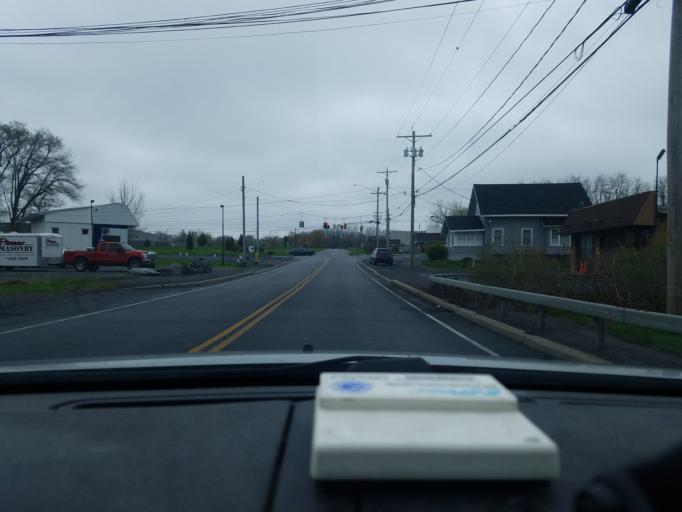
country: US
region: New York
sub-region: Onondaga County
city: North Syracuse
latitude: 43.1256
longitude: -76.0994
